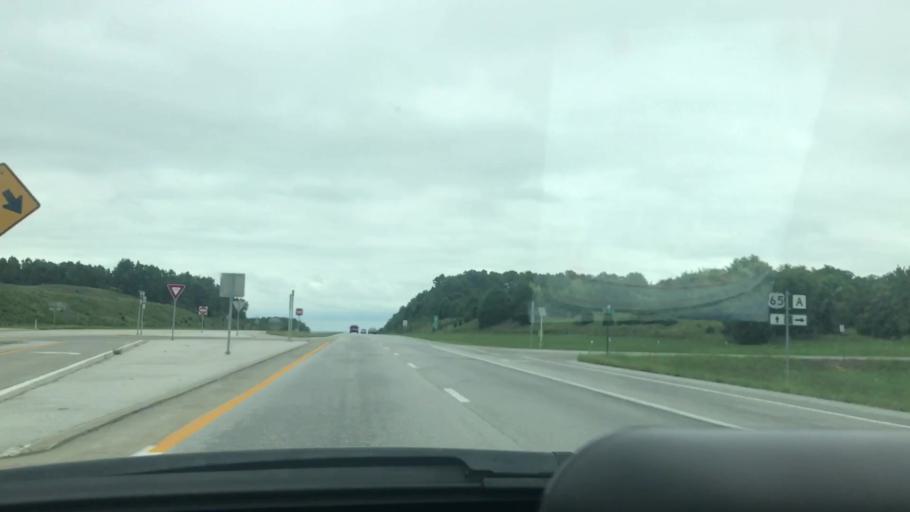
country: US
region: Missouri
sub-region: Greene County
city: Fair Grove
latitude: 37.3276
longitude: -93.1680
